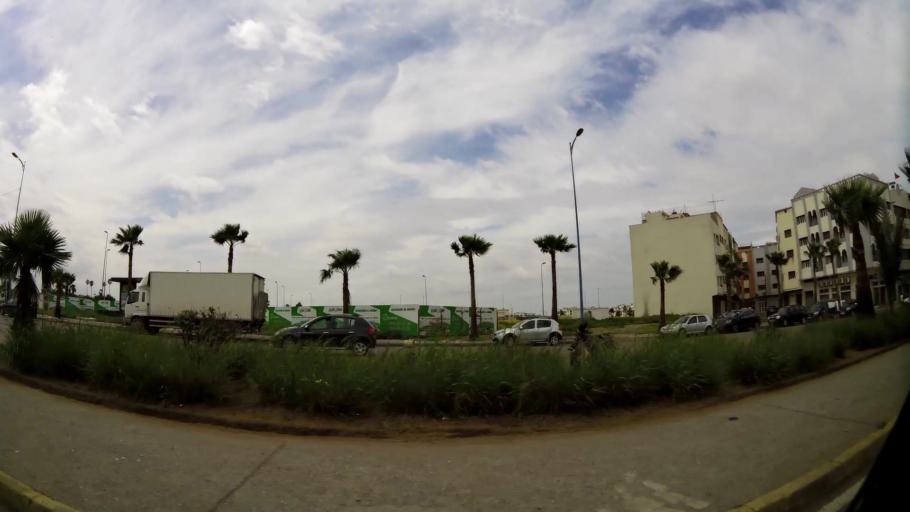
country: MA
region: Grand Casablanca
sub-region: Casablanca
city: Casablanca
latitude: 33.5822
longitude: -7.5707
